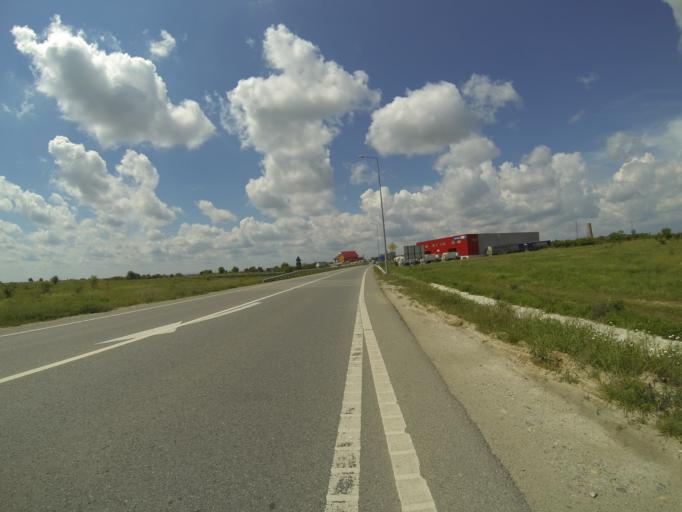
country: RO
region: Dolj
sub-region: Comuna Carcea
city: Carcea
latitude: 44.2615
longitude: 23.9051
